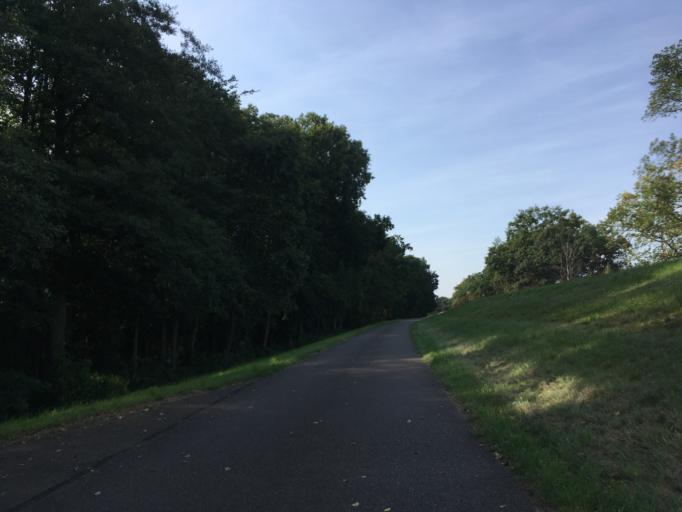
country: DE
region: Brandenburg
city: Wiesenau
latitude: 52.2621
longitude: 14.6363
